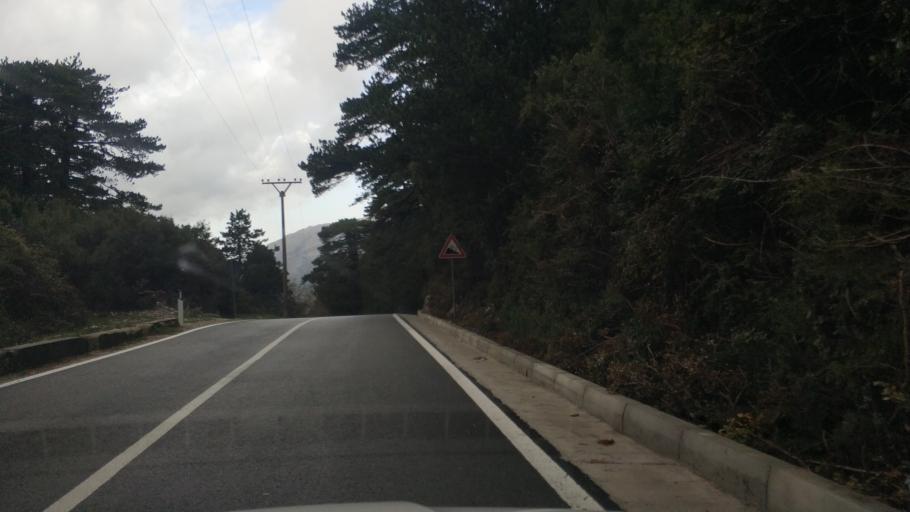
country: AL
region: Vlore
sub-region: Rrethi i Vlores
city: Brataj
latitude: 40.2174
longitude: 19.5792
